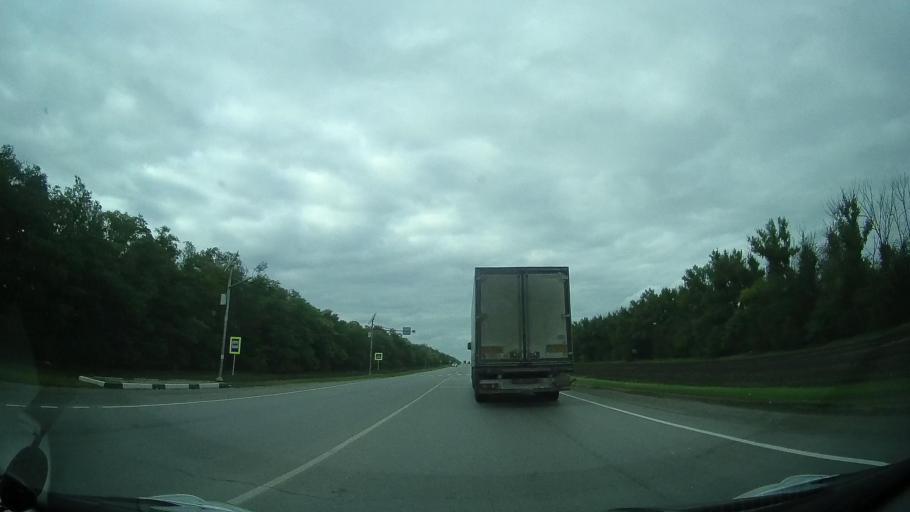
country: RU
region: Rostov
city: Yegorlykskaya
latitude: 46.6260
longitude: 40.5923
